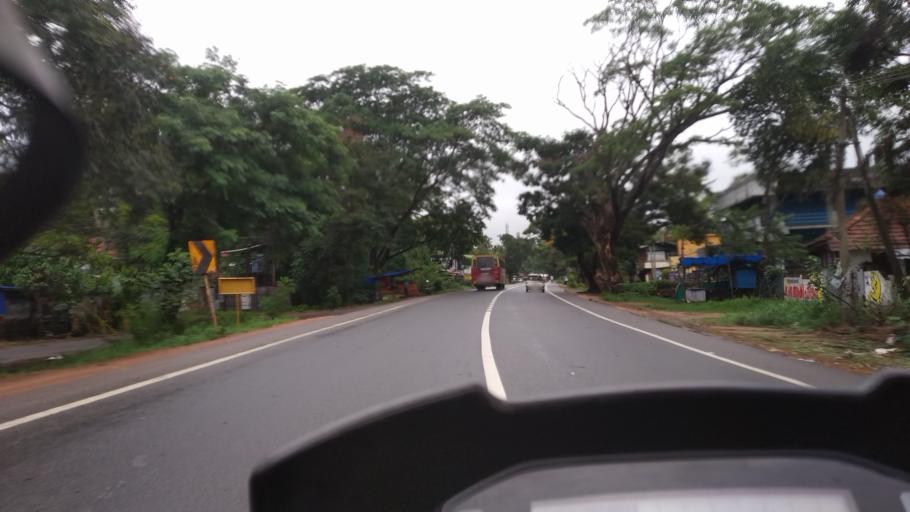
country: IN
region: Kerala
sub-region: Alappuzha
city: Mavelikara
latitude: 9.2850
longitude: 76.4398
